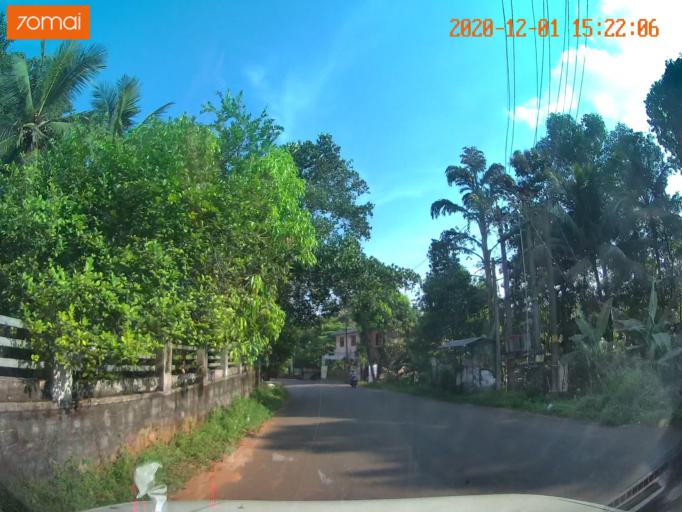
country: IN
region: Kerala
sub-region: Ernakulam
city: Muvattupuzha
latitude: 9.9459
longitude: 76.5464
